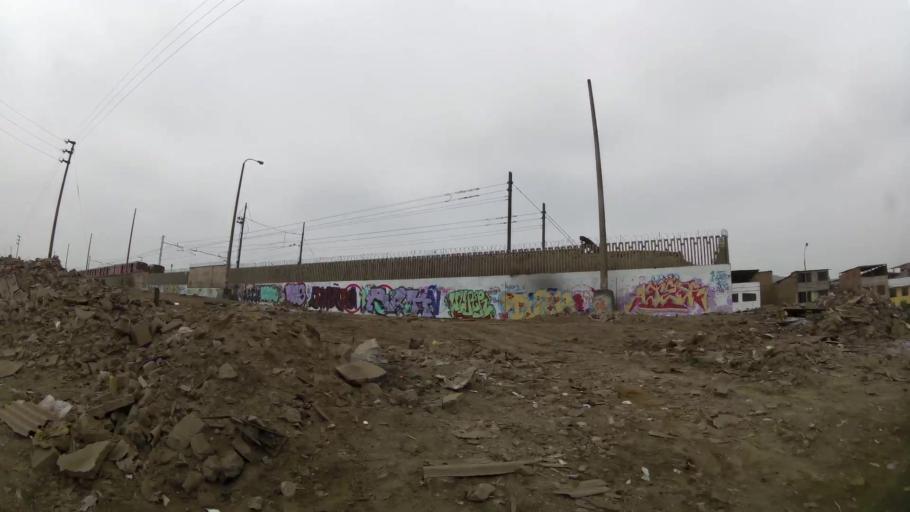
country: PE
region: Lima
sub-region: Lima
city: Surco
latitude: -12.2150
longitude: -76.9280
